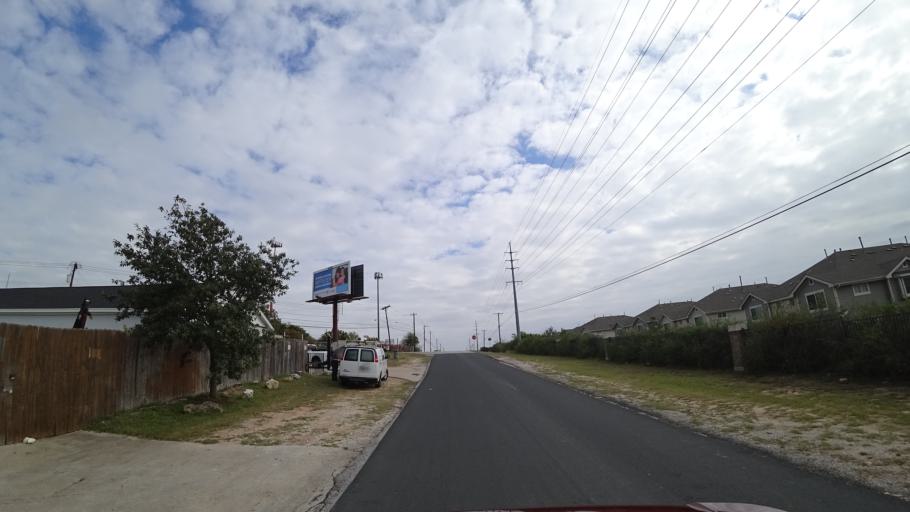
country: US
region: Texas
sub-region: Travis County
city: Wells Branch
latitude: 30.4311
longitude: -97.6853
